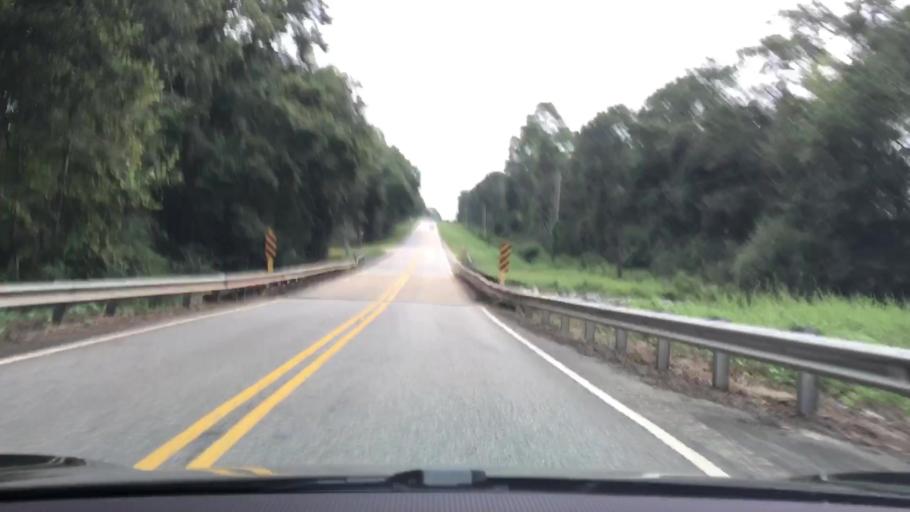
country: US
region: Alabama
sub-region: Covington County
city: Opp
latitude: 31.2960
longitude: -86.1434
